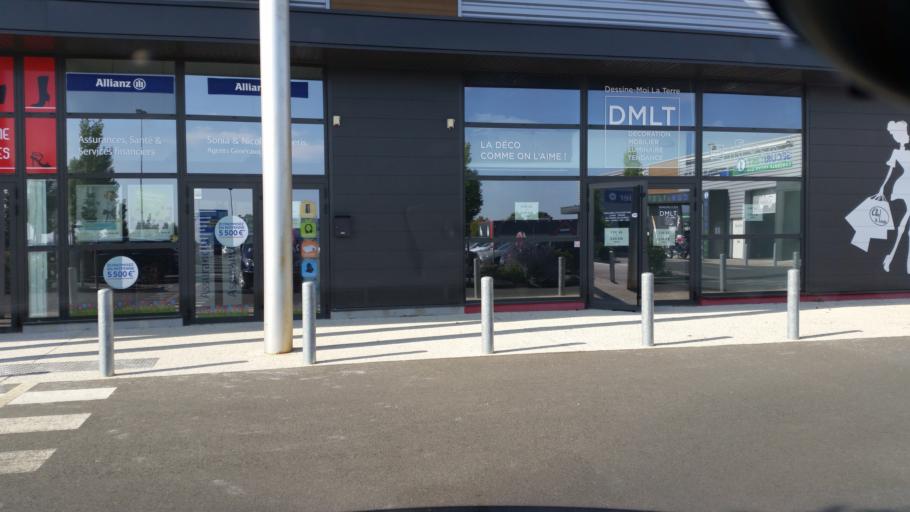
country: FR
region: Poitou-Charentes
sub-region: Departement de la Charente-Maritime
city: Saint-Jean-de-Liversay
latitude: 46.2285
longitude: -0.8748
